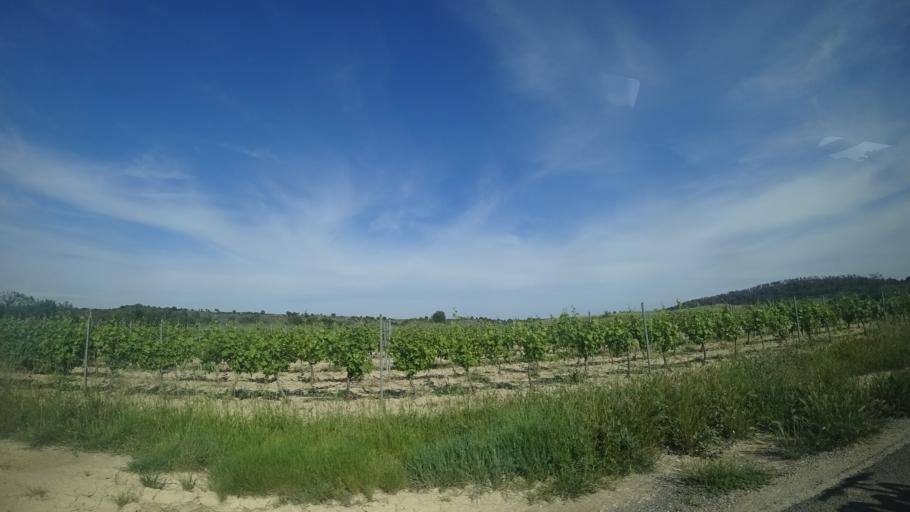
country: FR
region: Languedoc-Roussillon
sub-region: Departement de l'Aude
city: Ginestas
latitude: 43.2728
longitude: 2.8146
